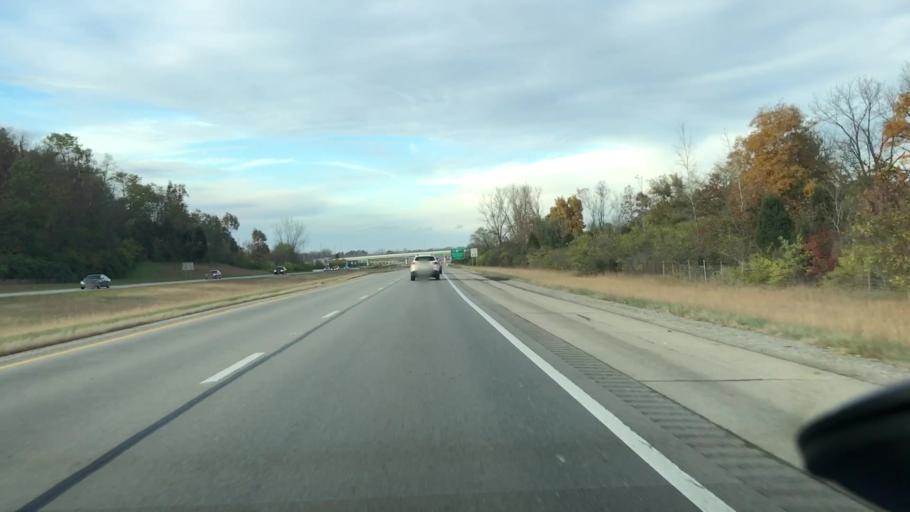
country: US
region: Ohio
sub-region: Clark County
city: Holiday Valley
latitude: 39.8530
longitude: -83.9941
